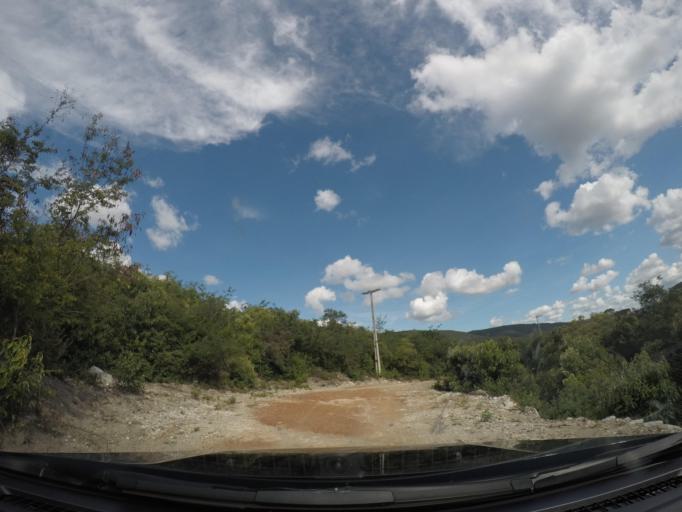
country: BR
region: Bahia
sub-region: Barra Da Estiva
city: Barra da Estiva
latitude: -13.1482
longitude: -41.5977
